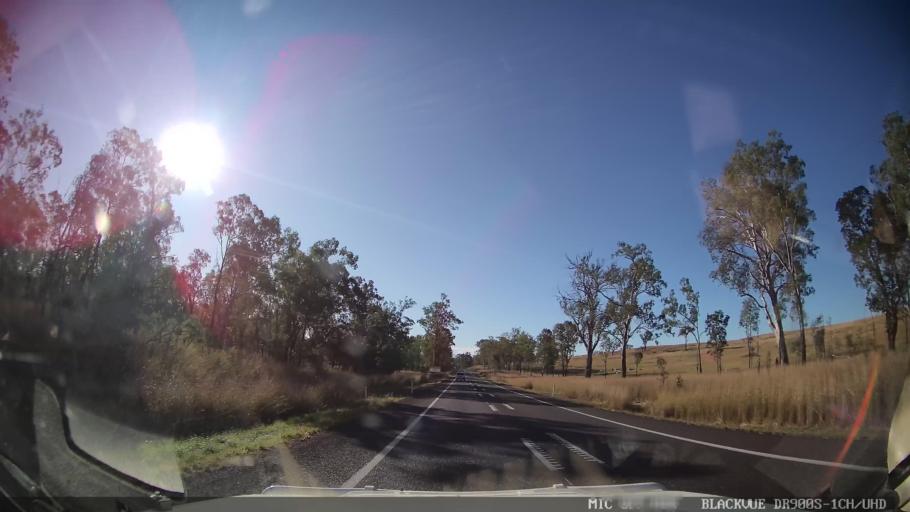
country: AU
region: Queensland
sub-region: Bundaberg
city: Sharon
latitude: -24.8342
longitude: 151.7095
